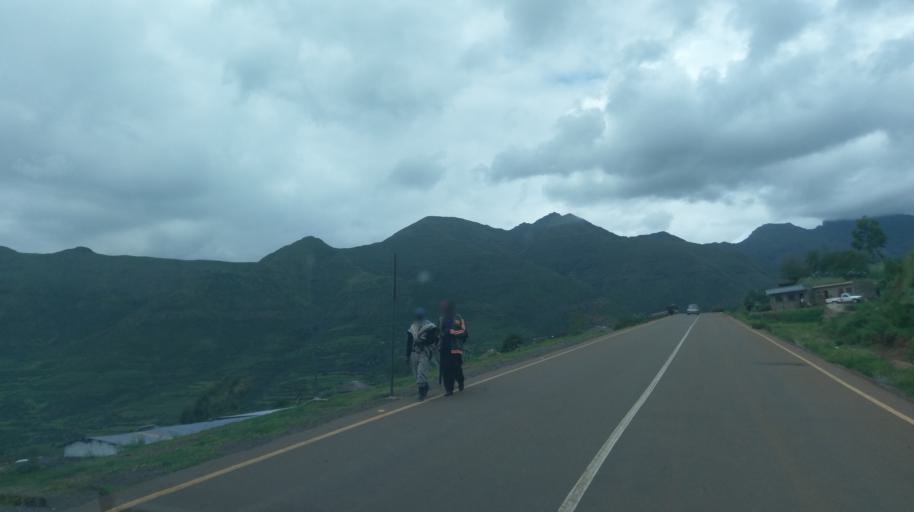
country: LS
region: Butha-Buthe
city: Butha-Buthe
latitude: -29.0447
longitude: 28.3151
